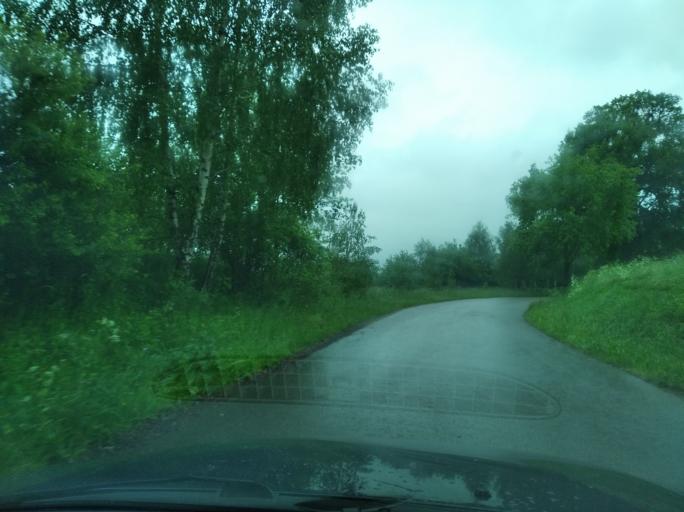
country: PL
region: Subcarpathian Voivodeship
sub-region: Powiat jasielski
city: Tarnowiec
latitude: 49.7736
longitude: 21.5476
